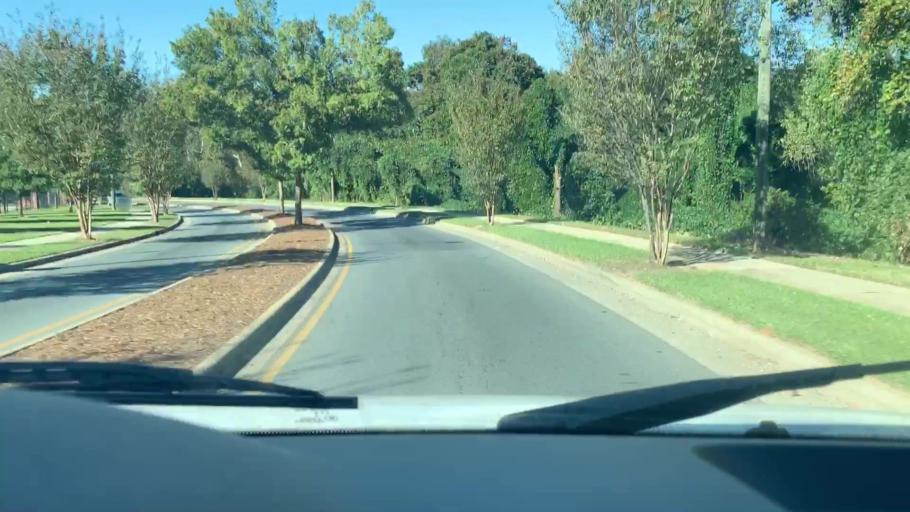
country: US
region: North Carolina
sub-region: Mecklenburg County
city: Charlotte
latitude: 35.2637
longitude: -80.8318
